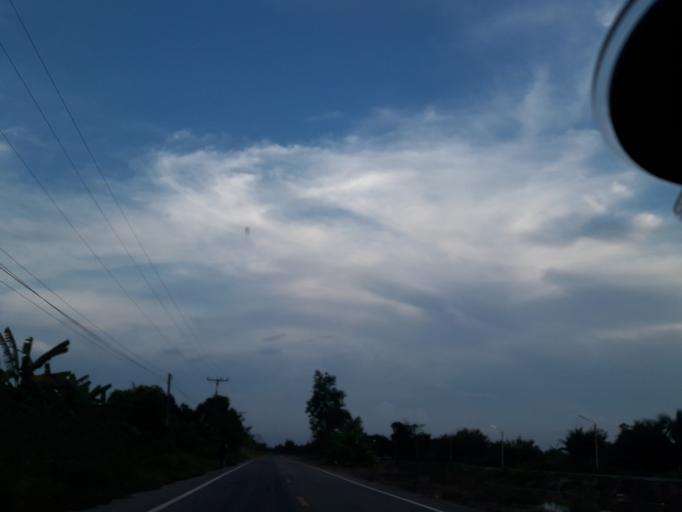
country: TH
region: Sara Buri
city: Nong Khae
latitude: 14.2522
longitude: 100.8688
